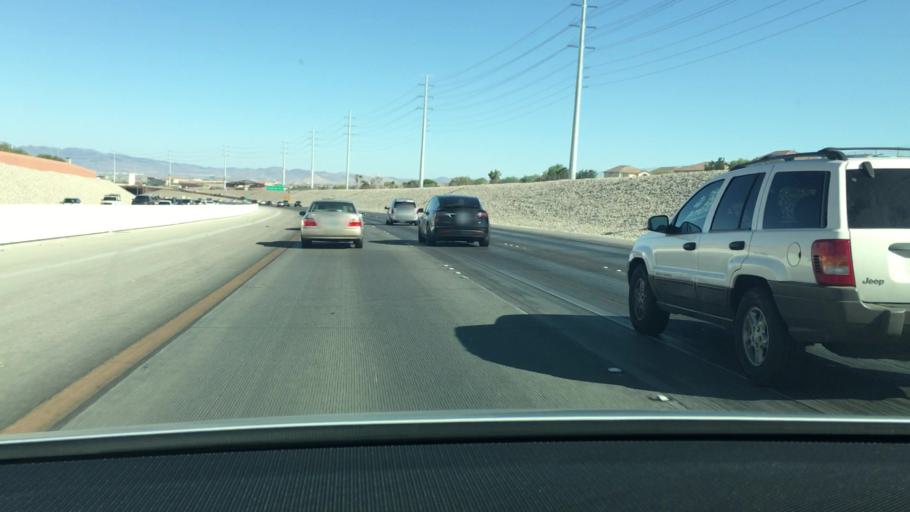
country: US
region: Nevada
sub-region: Clark County
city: Summerlin South
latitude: 36.1272
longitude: -115.3335
